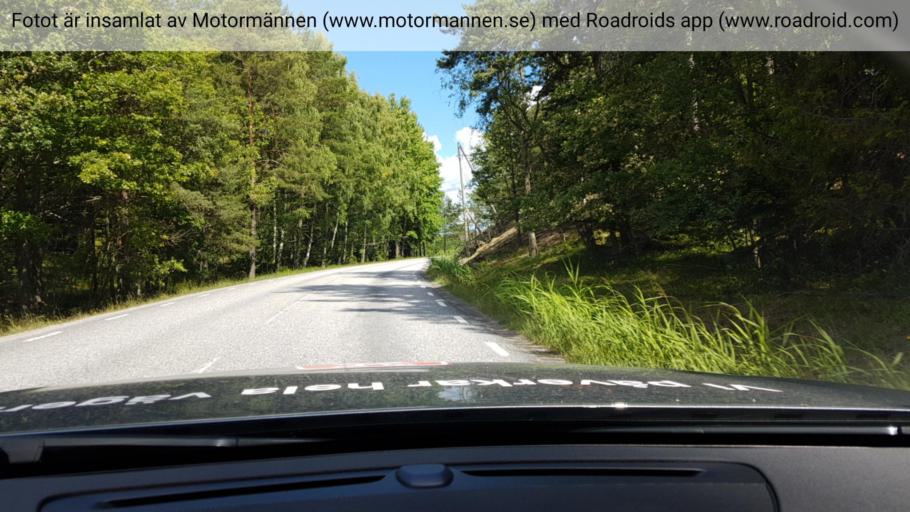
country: SE
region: Stockholm
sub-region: Varmdo Kommun
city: Hemmesta
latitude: 59.3654
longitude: 18.5197
